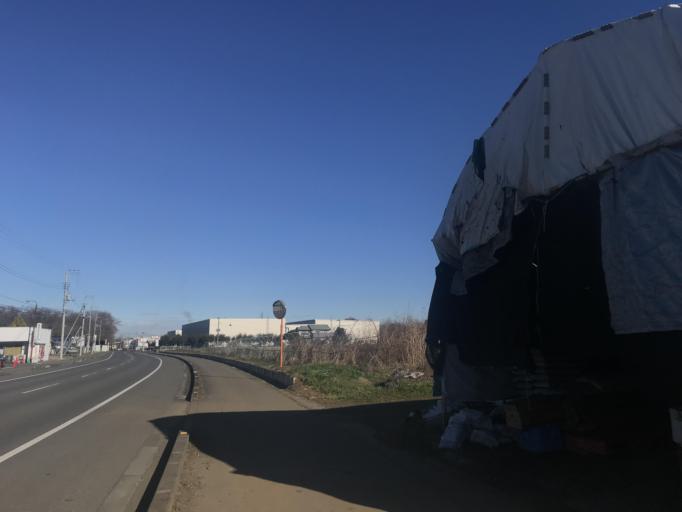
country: JP
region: Ibaraki
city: Yuki
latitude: 36.3211
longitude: 139.8794
